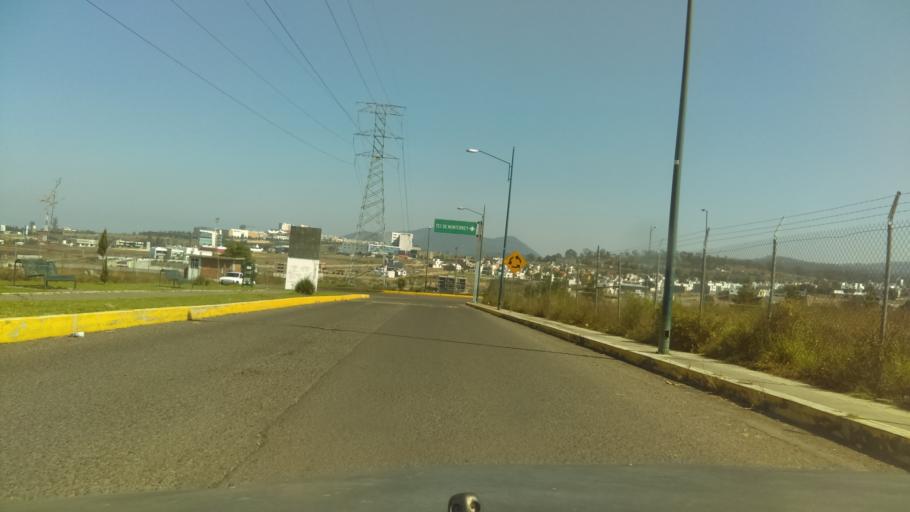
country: MX
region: Michoacan
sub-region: Morelia
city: Montana Monarca (Punta Altozano)
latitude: 19.6594
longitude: -101.1731
